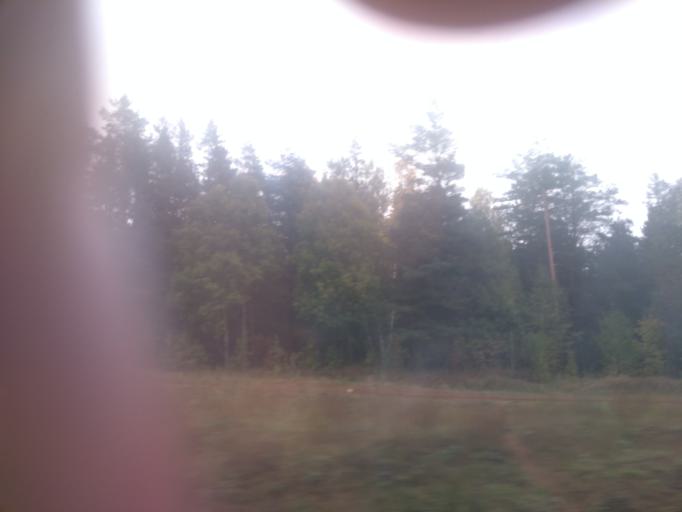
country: RU
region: Tatarstan
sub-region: Tukayevskiy Rayon
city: Naberezhnyye Chelny
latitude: 55.7277
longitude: 52.2568
